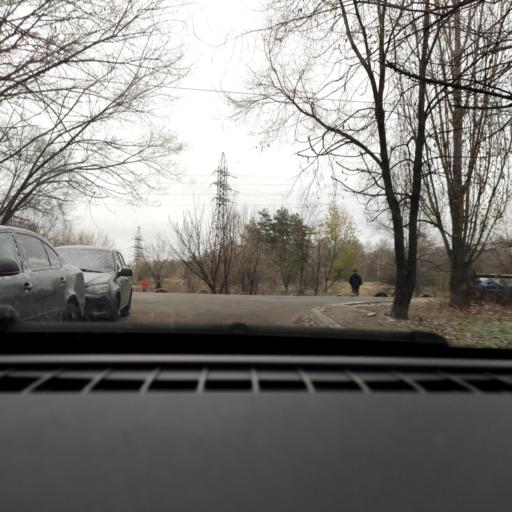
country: RU
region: Voronezj
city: Somovo
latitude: 51.7349
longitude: 39.2959
